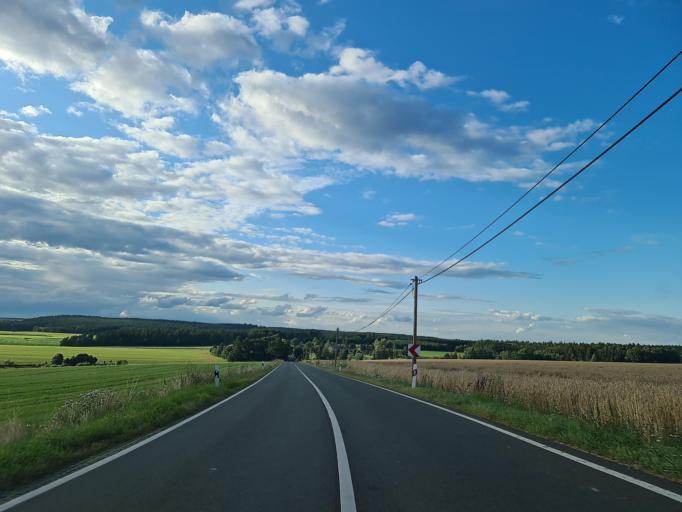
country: DE
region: Saxony
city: Pausa
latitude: 50.5927
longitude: 11.9981
